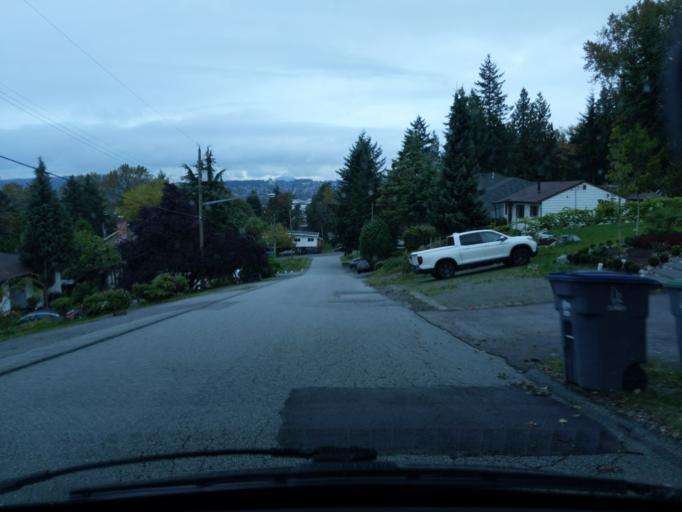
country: CA
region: British Columbia
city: New Westminster
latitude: 49.2035
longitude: -122.8619
